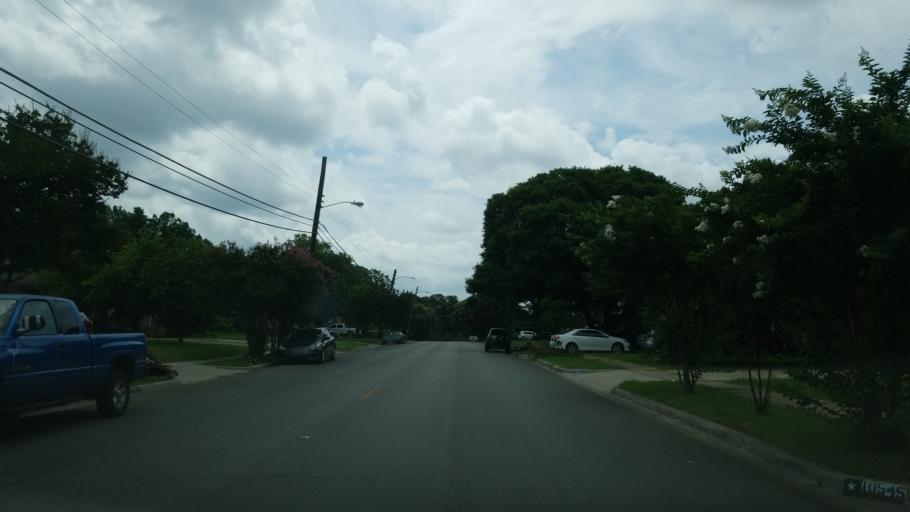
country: US
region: Texas
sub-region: Dallas County
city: Farmers Branch
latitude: 32.8914
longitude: -96.8785
